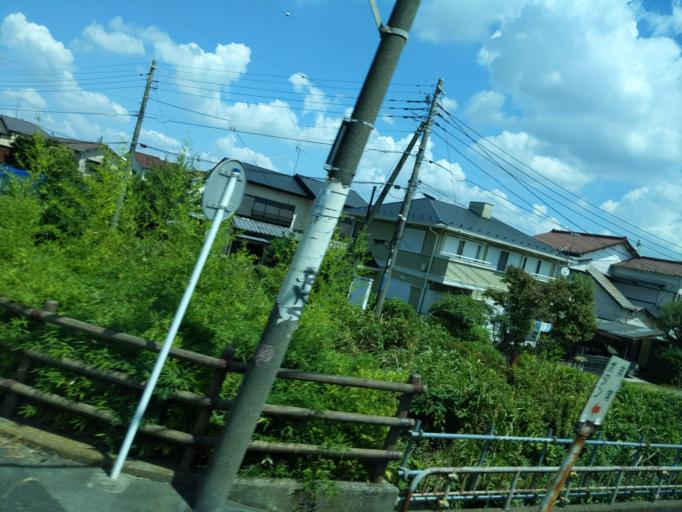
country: JP
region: Tokyo
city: Chofugaoka
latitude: 35.6315
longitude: 139.5446
